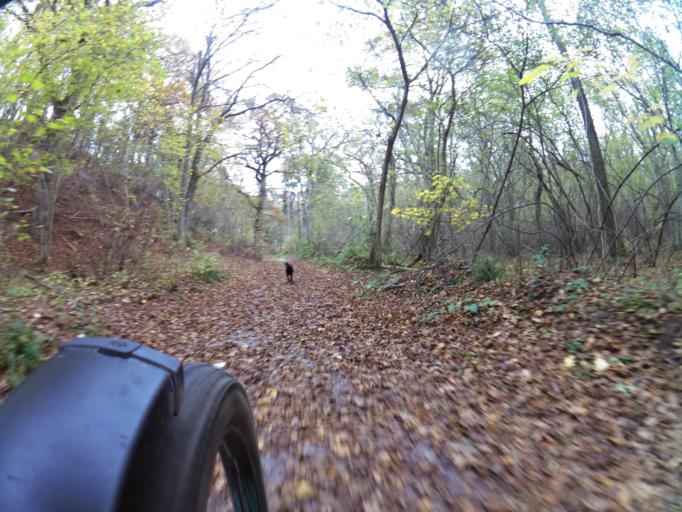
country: PL
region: Pomeranian Voivodeship
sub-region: Powiat pucki
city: Krokowa
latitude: 54.8307
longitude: 18.1114
